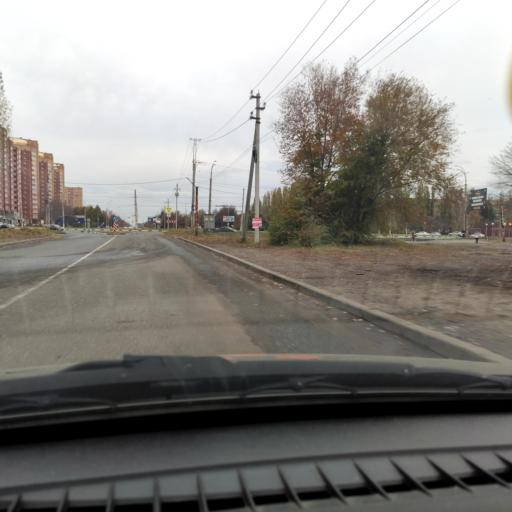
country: RU
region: Samara
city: Tol'yatti
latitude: 53.5168
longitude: 49.3124
